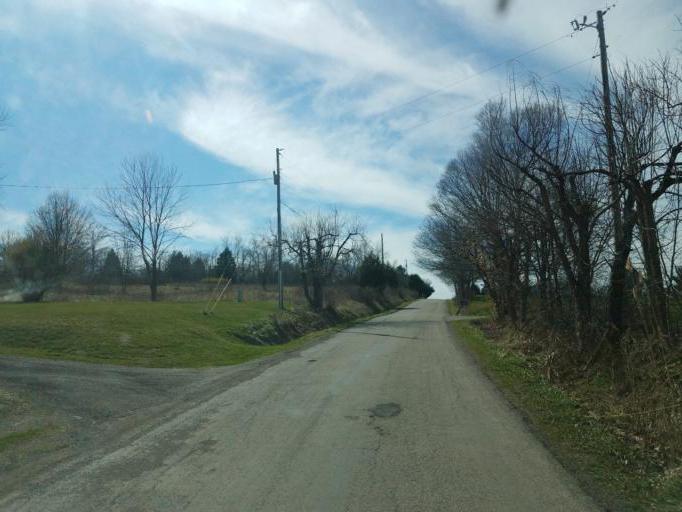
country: US
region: Ohio
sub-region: Richland County
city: Lincoln Heights
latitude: 40.8070
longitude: -82.4700
